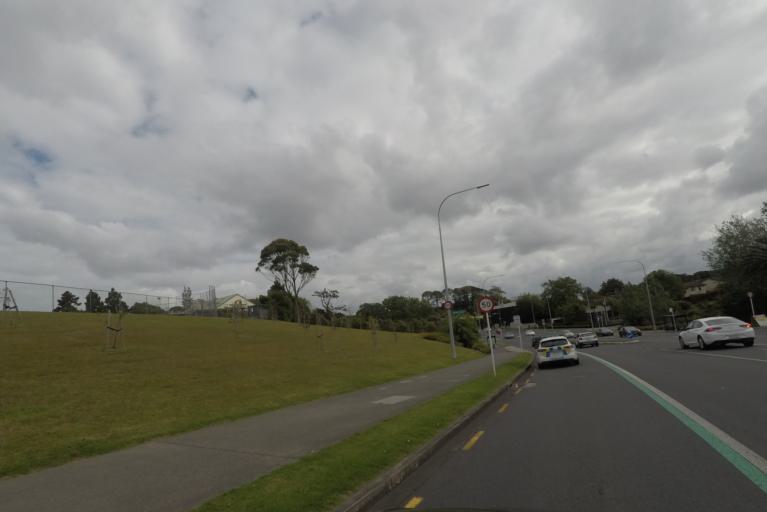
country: NZ
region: Auckland
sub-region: Auckland
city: Rothesay Bay
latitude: -36.7278
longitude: 174.6976
